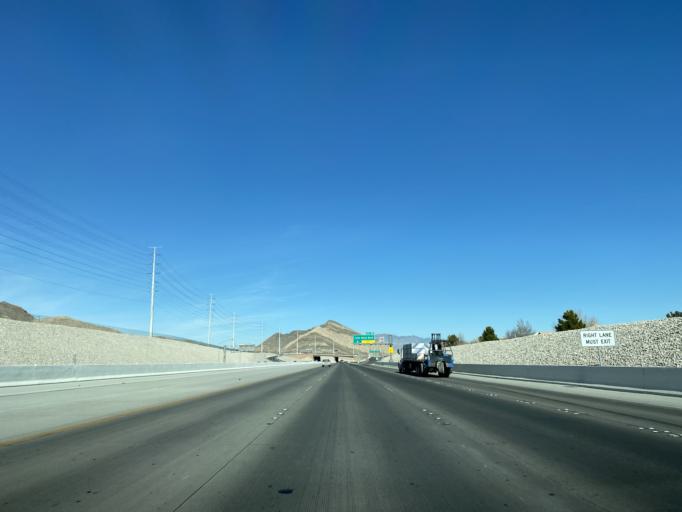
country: US
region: Nevada
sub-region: Clark County
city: Summerlin South
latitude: 36.1990
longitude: -115.3414
